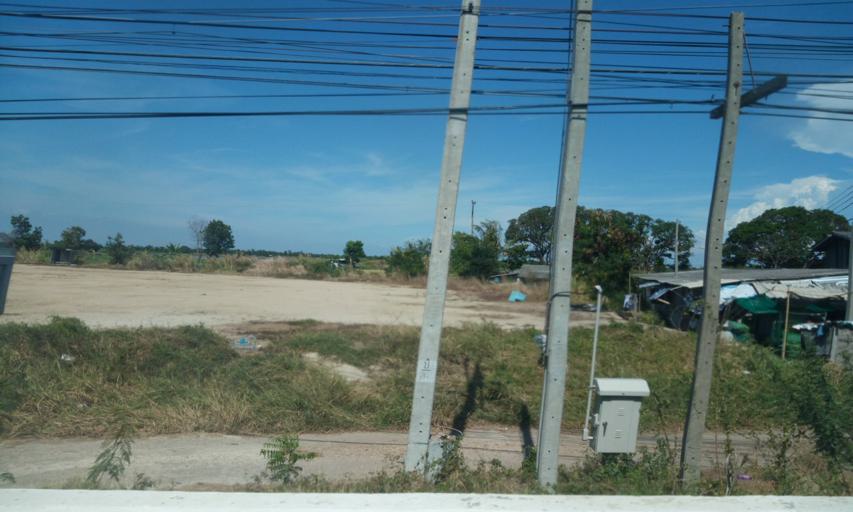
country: TH
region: Samut Prakan
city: Bang Bo District
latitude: 13.5165
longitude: 100.7886
